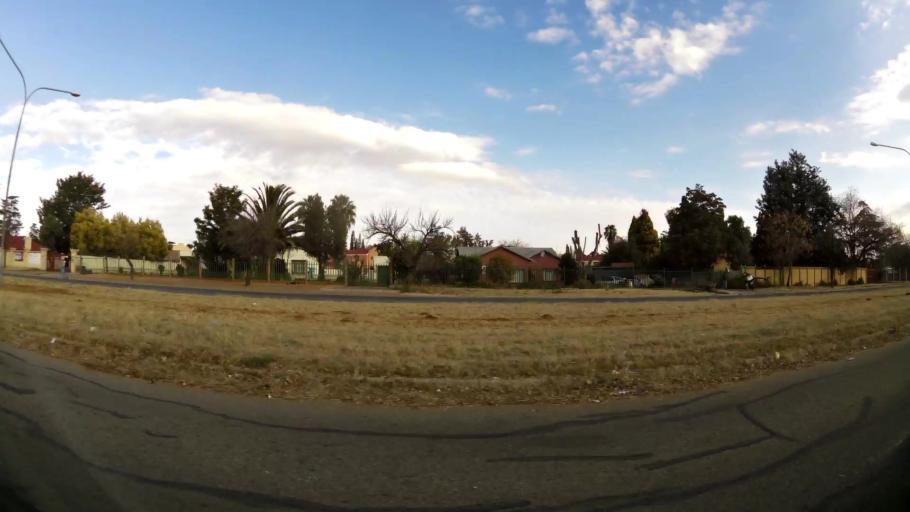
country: ZA
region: Orange Free State
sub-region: Lejweleputswa District Municipality
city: Welkom
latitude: -27.9890
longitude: 26.7193
